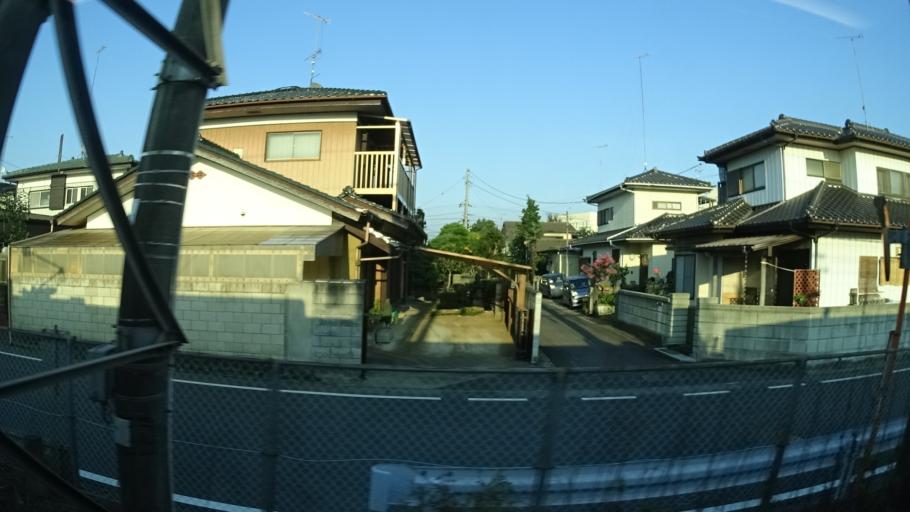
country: JP
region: Ibaraki
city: Tomobe
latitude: 36.3440
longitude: 140.2993
